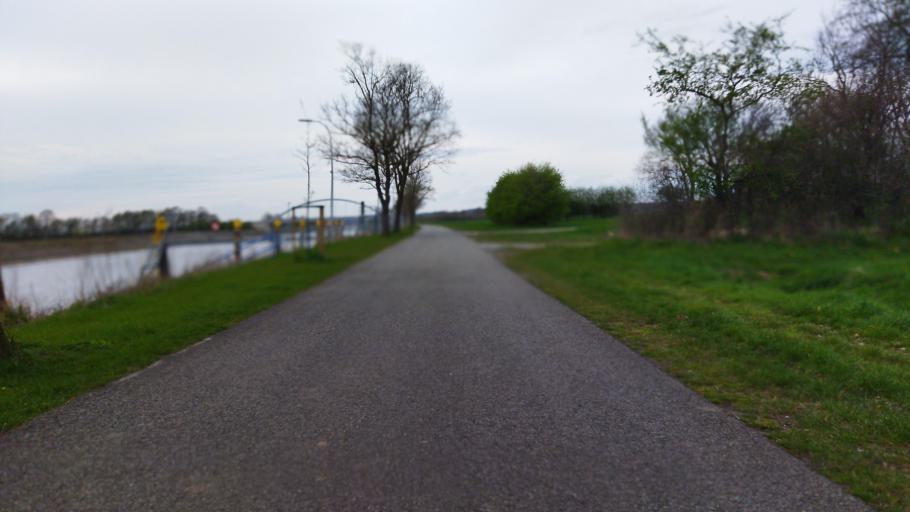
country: DE
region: Lower Saxony
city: Ahsen-Oetzen
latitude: 52.9856
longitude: 9.1160
